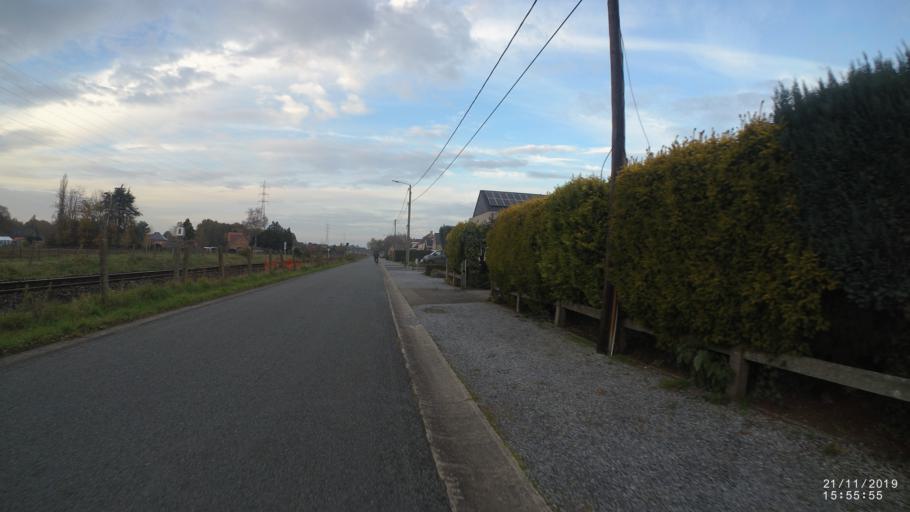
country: BE
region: Flanders
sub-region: Provincie Limburg
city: Zonhoven
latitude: 50.9976
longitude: 5.3485
